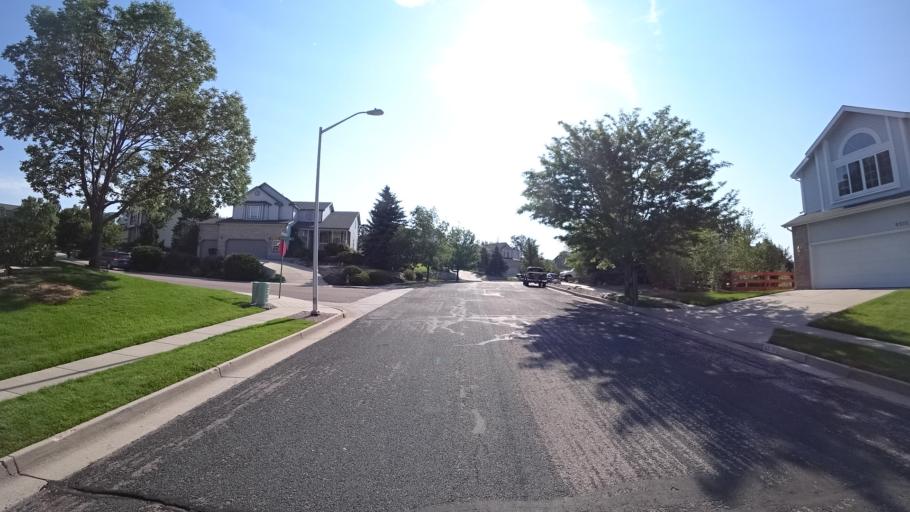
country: US
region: Colorado
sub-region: El Paso County
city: Air Force Academy
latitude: 38.9506
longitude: -104.7829
